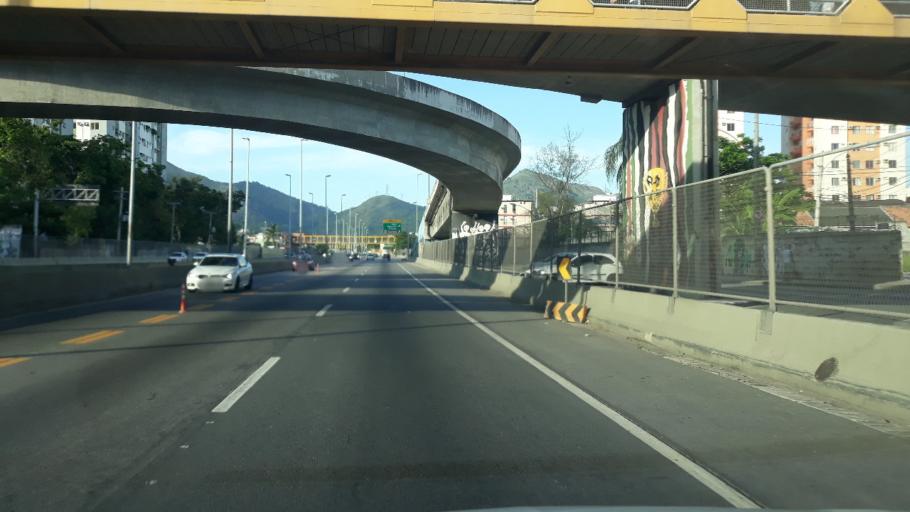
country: BR
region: Rio de Janeiro
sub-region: Rio De Janeiro
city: Rio de Janeiro
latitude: -22.8890
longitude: -43.2952
